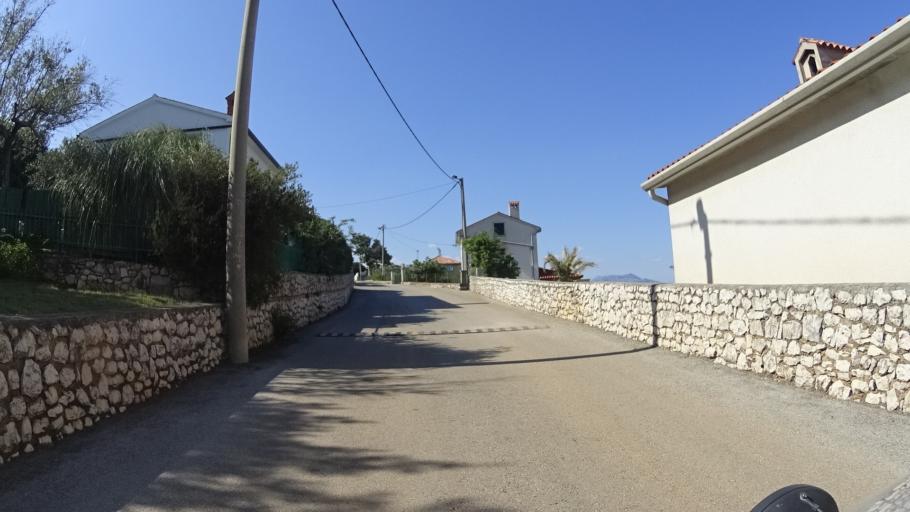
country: HR
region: Istarska
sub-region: Grad Labin
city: Rabac
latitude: 44.9998
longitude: 14.1636
